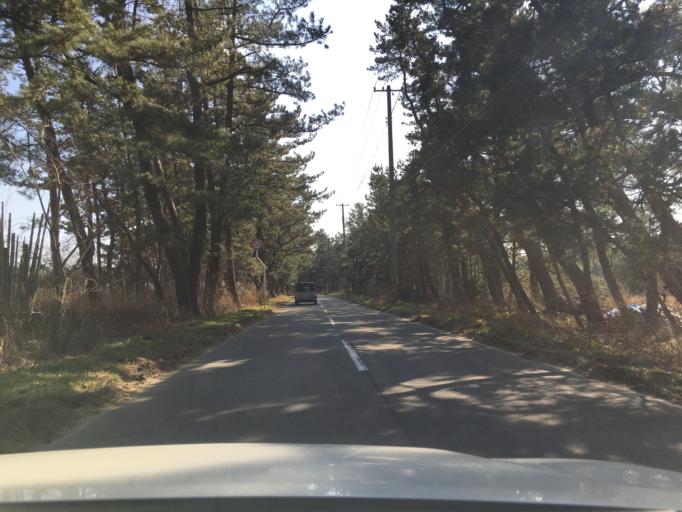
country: JP
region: Yamagata
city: Tsuruoka
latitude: 38.8177
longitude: 139.7786
